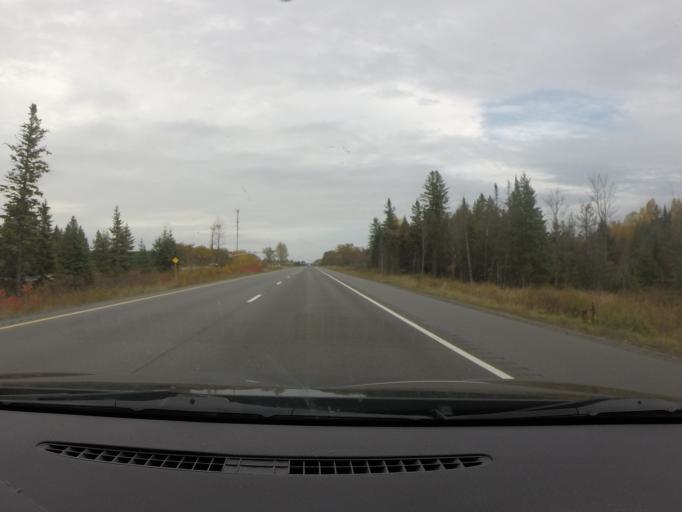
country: CA
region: Ontario
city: Carleton Place
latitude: 45.3233
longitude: -76.1127
